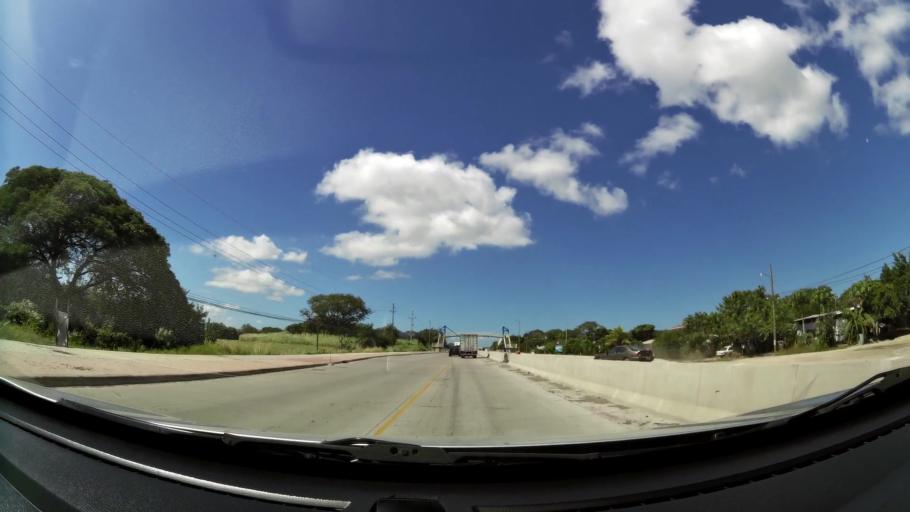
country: CR
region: Guanacaste
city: Bagaces
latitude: 10.5194
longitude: -85.2477
